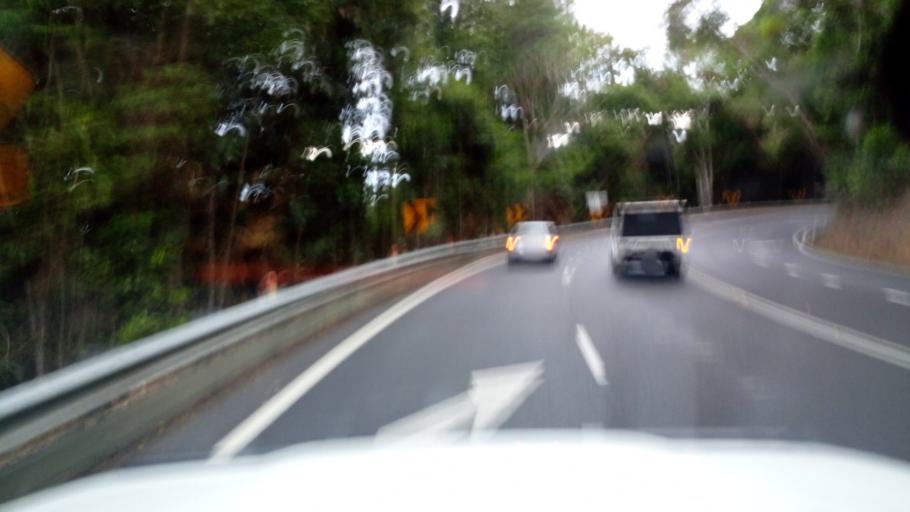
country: AU
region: Queensland
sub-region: Tablelands
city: Kuranda
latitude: -16.8303
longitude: 145.6675
